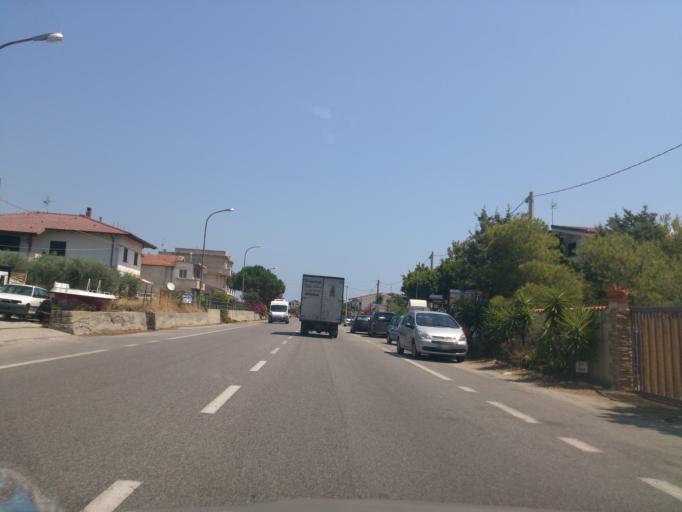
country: IT
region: Calabria
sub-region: Provincia di Reggio Calabria
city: Riace Marina
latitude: 38.3992
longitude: 16.5408
